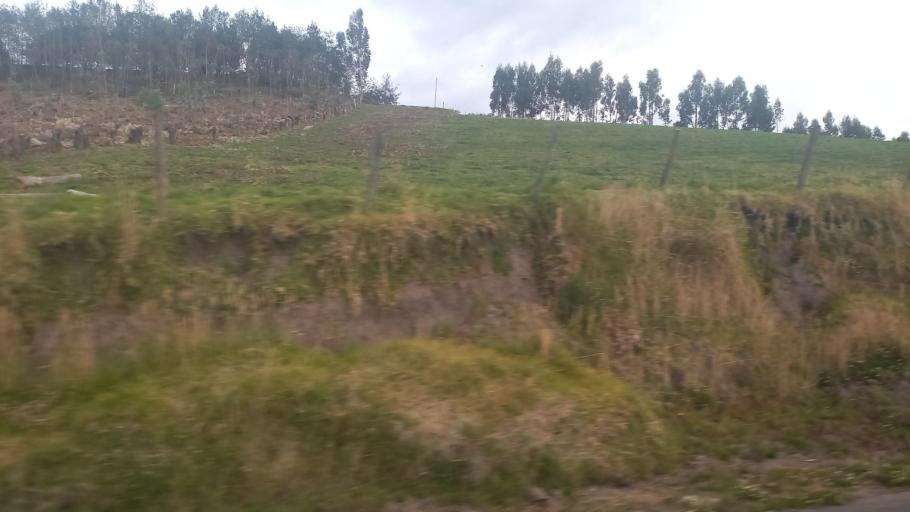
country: EC
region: Pichincha
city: Cayambe
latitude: 0.1008
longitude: -78.0867
